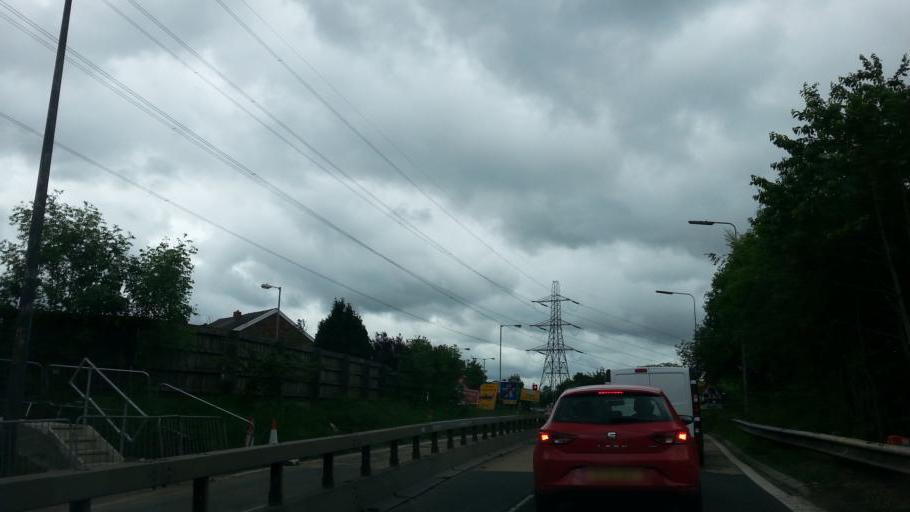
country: GB
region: England
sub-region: Borough of Bury
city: Prestwich
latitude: 53.5394
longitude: -2.2873
